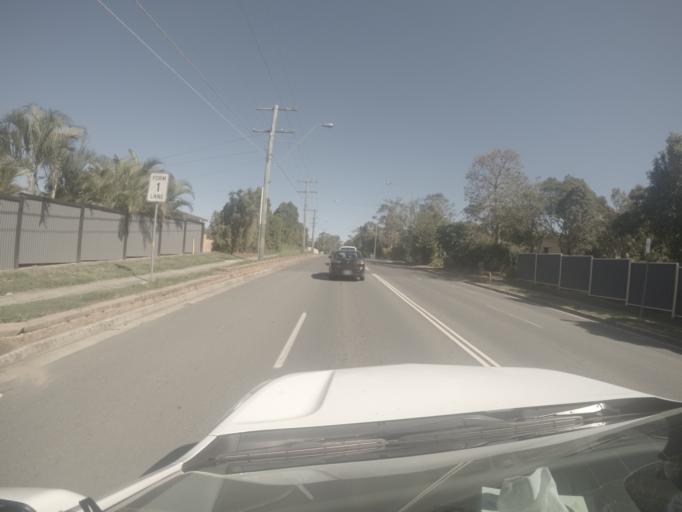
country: AU
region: Queensland
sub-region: Ipswich
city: Springfield
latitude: -27.6290
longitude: 152.9161
